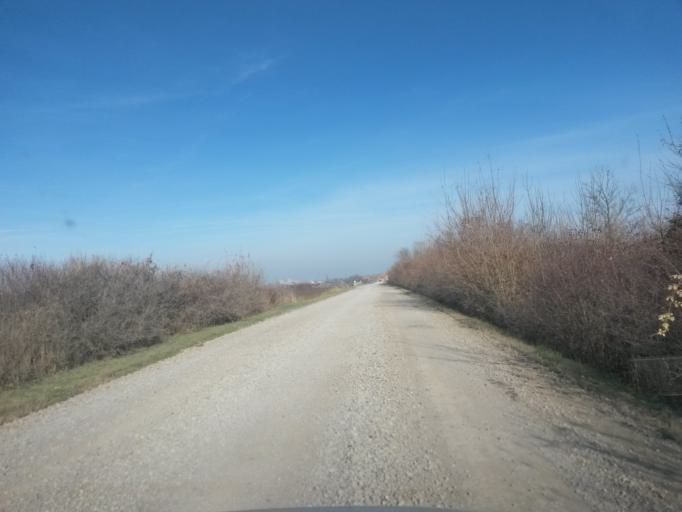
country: HR
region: Vukovarsko-Srijemska
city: Mirkovci
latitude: 45.2314
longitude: 18.8848
